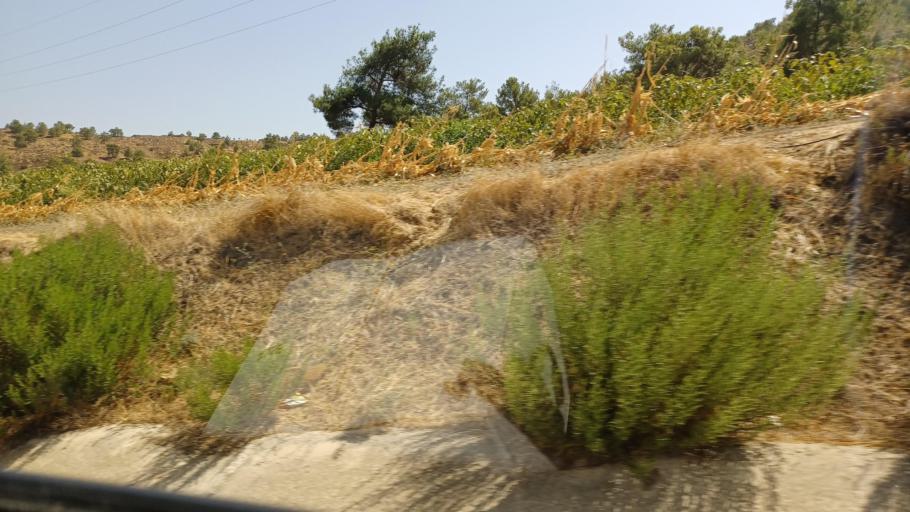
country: CY
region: Lefkosia
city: Lefka
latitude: 35.0587
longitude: 32.8957
